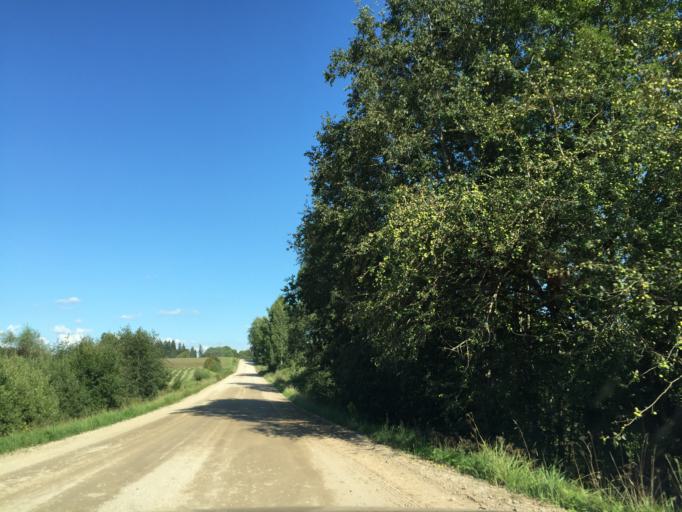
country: LV
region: Limbazu Rajons
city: Limbazi
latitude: 57.5502
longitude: 24.7732
